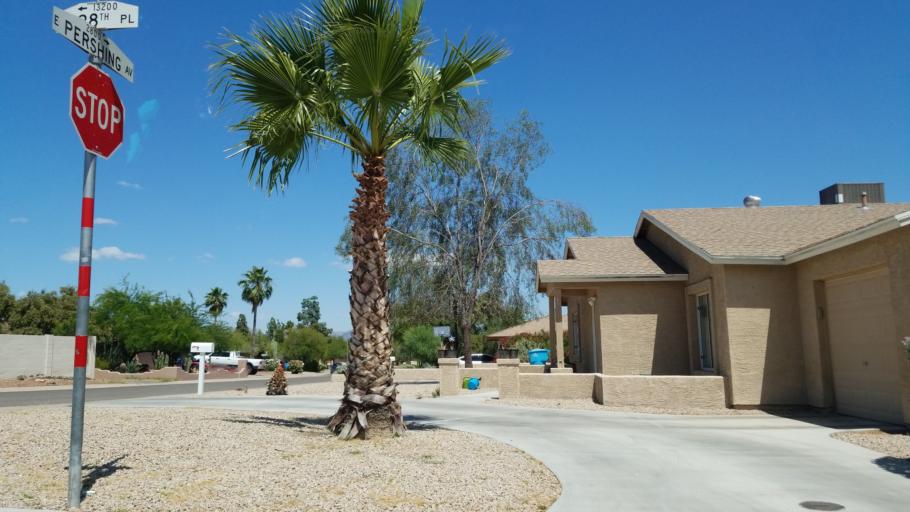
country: US
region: Arizona
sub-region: Maricopa County
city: Paradise Valley
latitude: 33.6060
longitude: -112.0210
